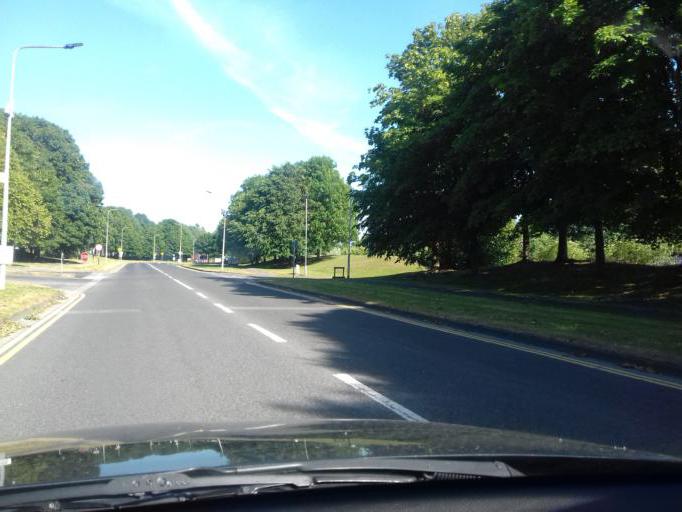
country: IE
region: Leinster
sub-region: Fingal County
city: Blanchardstown
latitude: 53.4031
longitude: -6.3664
